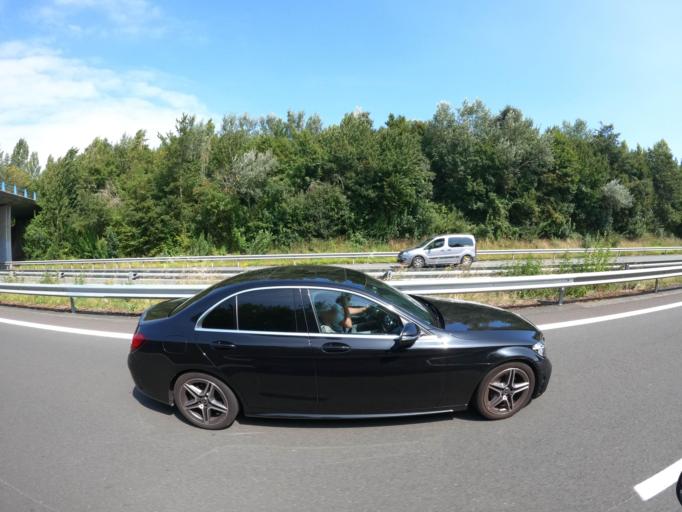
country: FR
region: Poitou-Charentes
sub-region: Departement des Deux-Sevres
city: Saint-Hilaire-la-Palud
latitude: 46.2114
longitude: -0.7498
